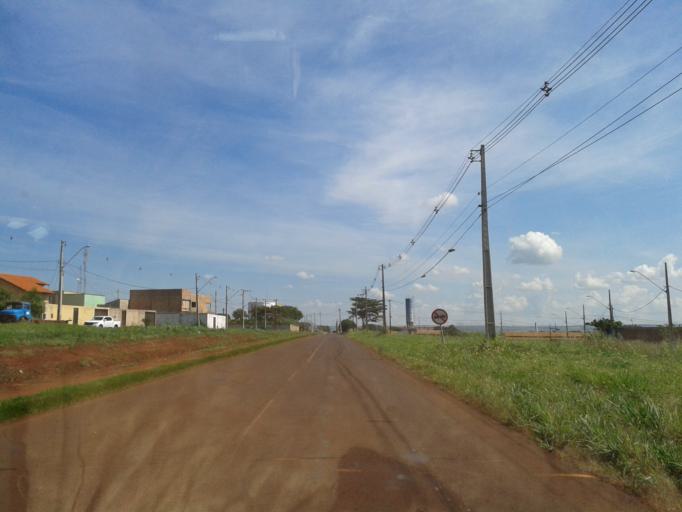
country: BR
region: Goias
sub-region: Itumbiara
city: Itumbiara
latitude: -18.4270
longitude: -49.1842
